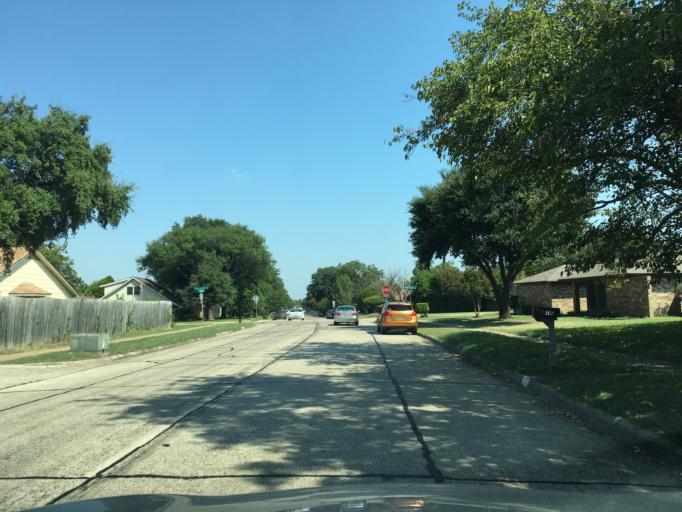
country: US
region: Texas
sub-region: Dallas County
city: Garland
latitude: 32.9376
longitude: -96.6572
